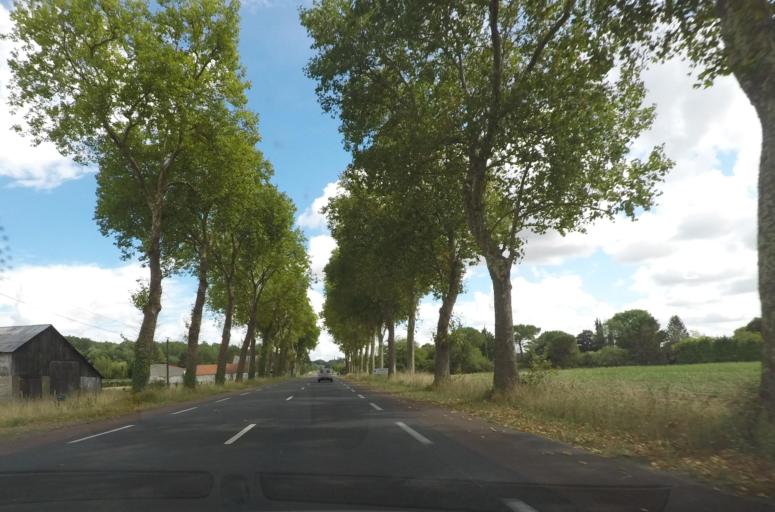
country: FR
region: Pays de la Loire
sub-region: Departement de la Sarthe
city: Clermont-Creans
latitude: 47.7076
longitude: -0.0438
